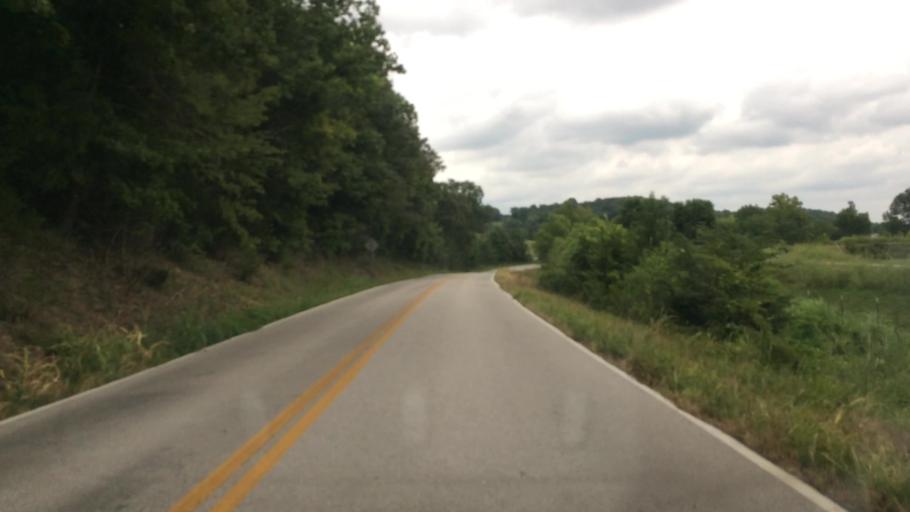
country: US
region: Missouri
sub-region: Greene County
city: Strafford
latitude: 37.2908
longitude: -93.0872
